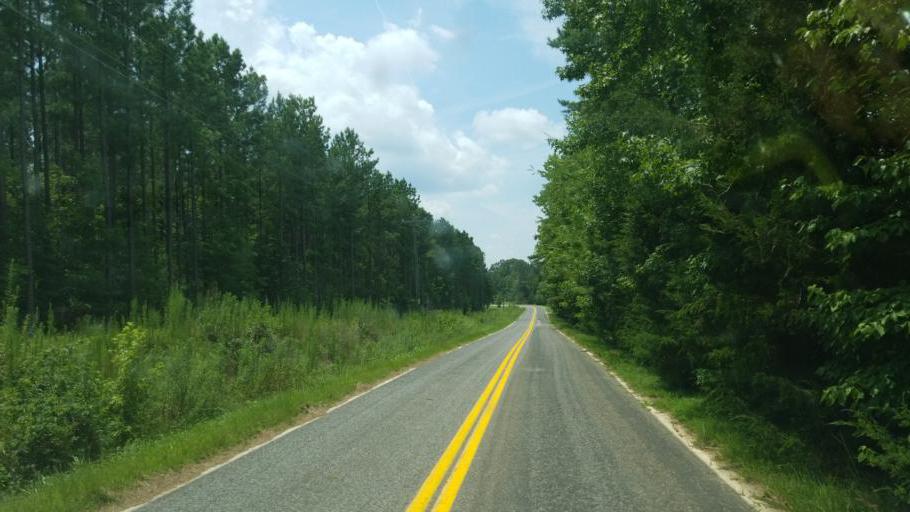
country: US
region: South Carolina
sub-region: Cherokee County
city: Blacksburg
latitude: 35.0957
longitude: -81.3949
